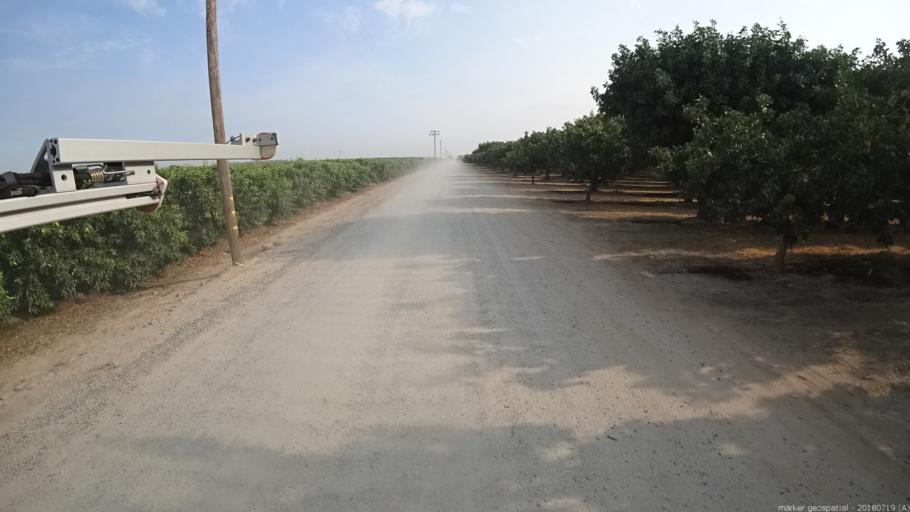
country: US
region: California
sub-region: Madera County
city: Fairmead
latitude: 37.1008
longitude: -120.1932
